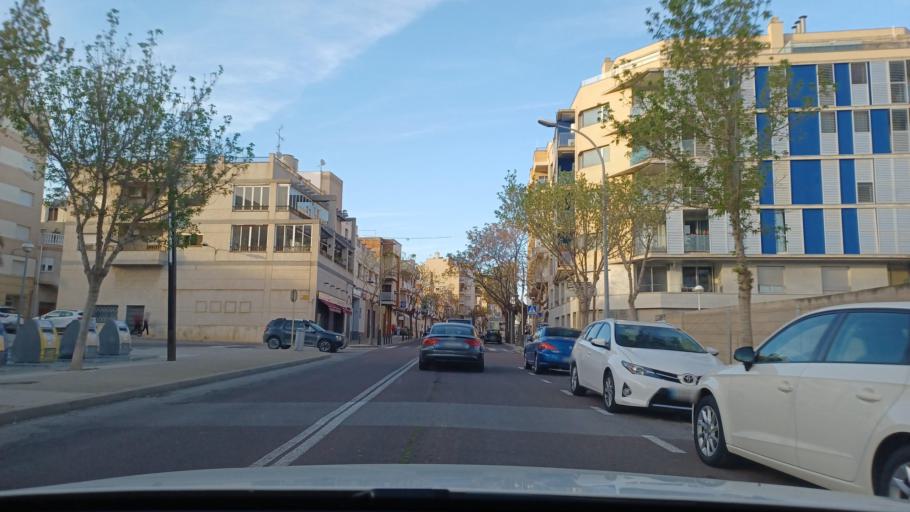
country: ES
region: Catalonia
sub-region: Provincia de Tarragona
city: Sant Carles de la Rapita
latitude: 40.6130
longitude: 0.5862
